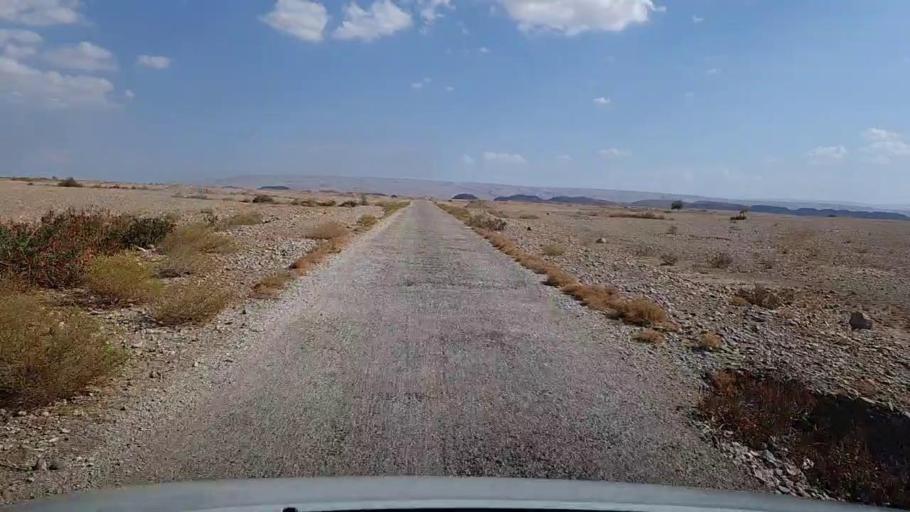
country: PK
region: Sindh
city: Bhan
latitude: 26.3663
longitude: 67.6404
